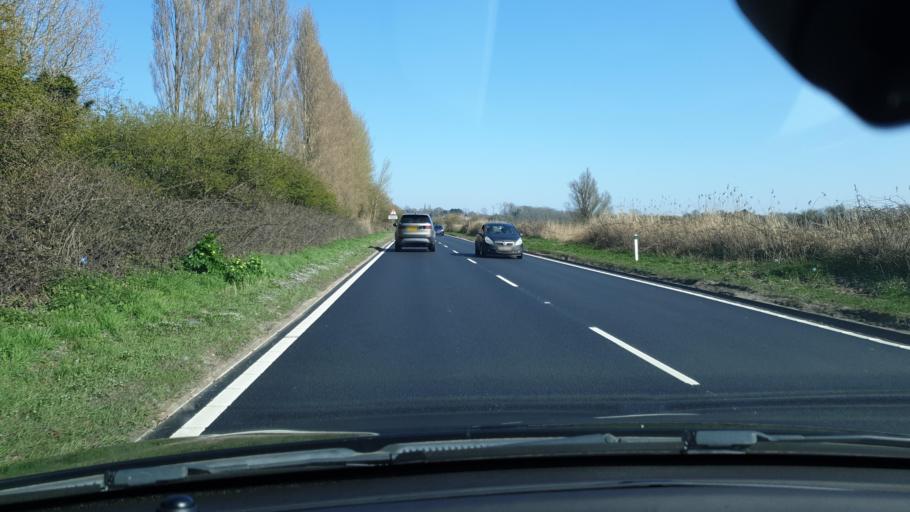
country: GB
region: England
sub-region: Suffolk
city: Shotley Gate
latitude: 51.9262
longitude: 1.2082
